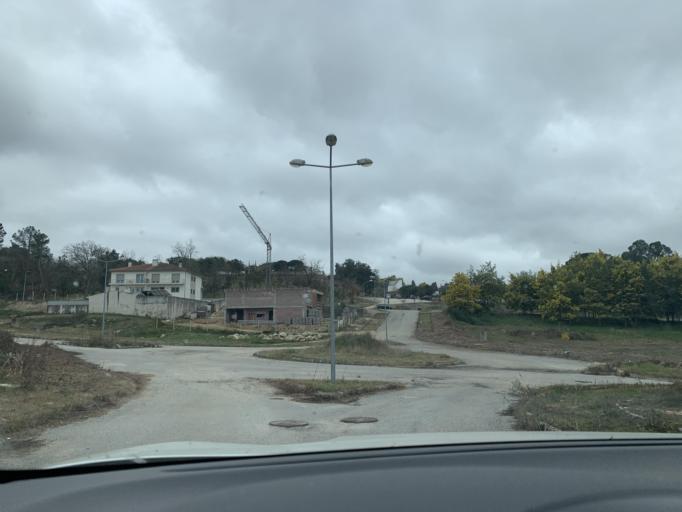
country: PT
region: Viseu
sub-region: Mangualde
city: Mangualde
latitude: 40.6099
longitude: -7.7690
